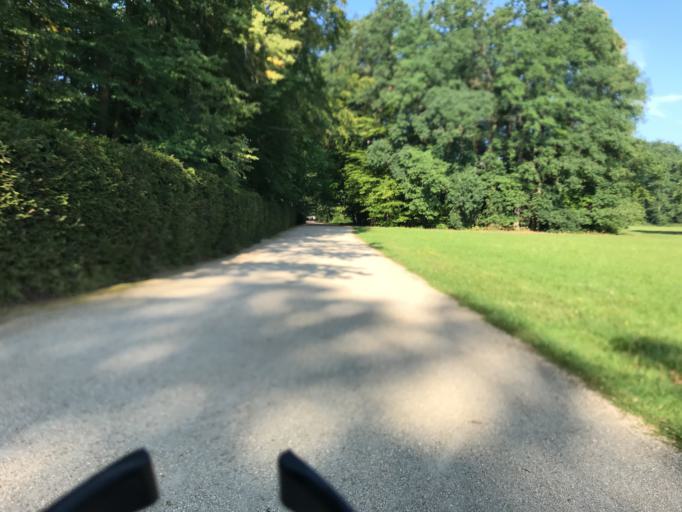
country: CZ
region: Jihocesky
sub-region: Okres Jindrichuv Hradec
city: Trebon
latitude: 48.9950
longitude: 14.7655
